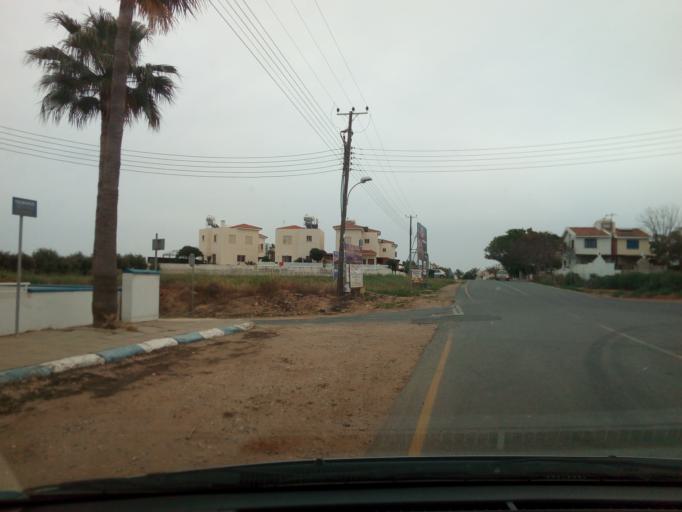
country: CY
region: Ammochostos
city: Paralimni
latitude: 35.0581
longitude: 34.0037
